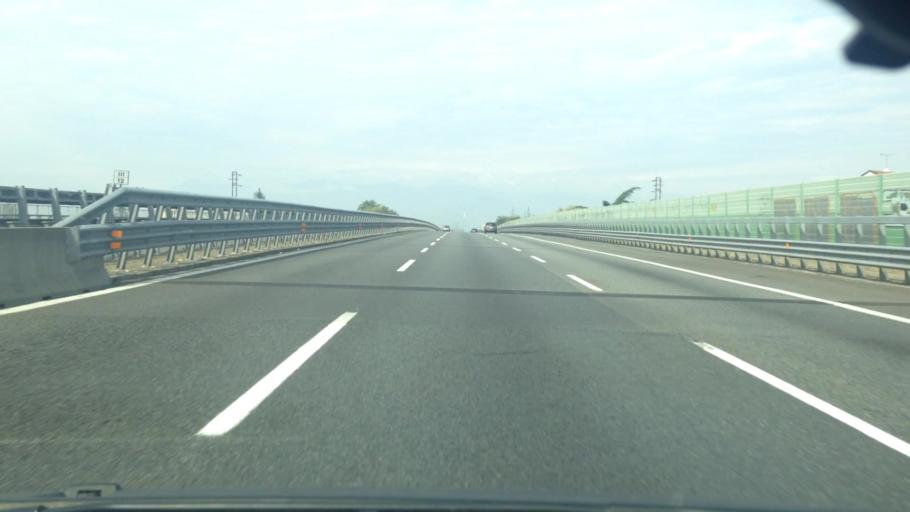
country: IT
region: Piedmont
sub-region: Provincia di Torino
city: Nichelino
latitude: 44.9864
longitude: 7.6382
